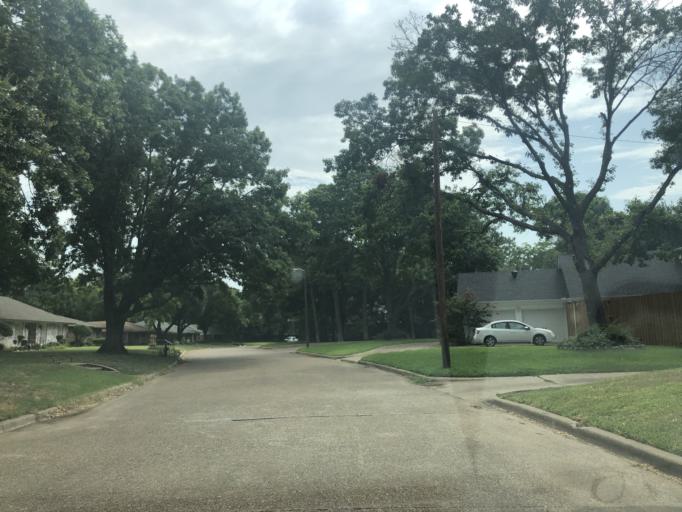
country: US
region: Texas
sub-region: Dallas County
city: Grand Prairie
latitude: 32.7652
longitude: -97.0181
